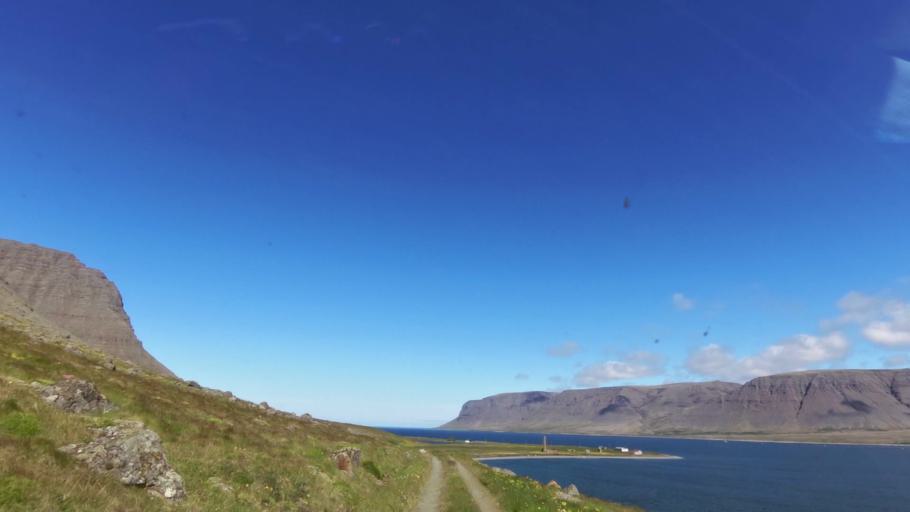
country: IS
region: West
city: Olafsvik
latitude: 65.6348
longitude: -23.9256
